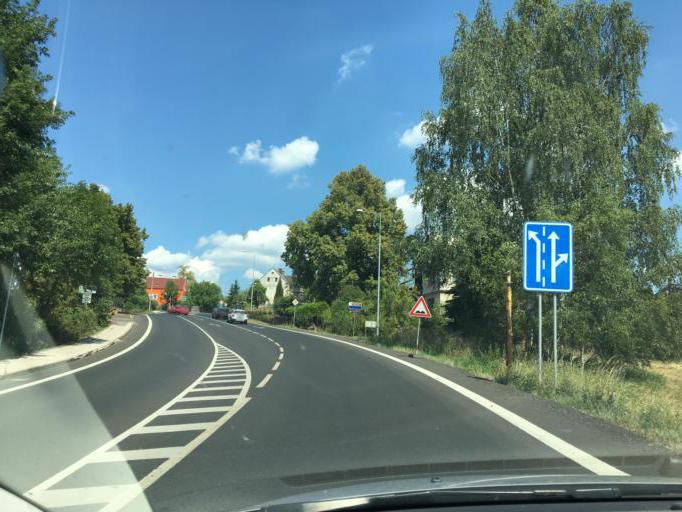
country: CZ
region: Ustecky
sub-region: Okres Decin
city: Decin
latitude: 50.7897
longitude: 14.2522
